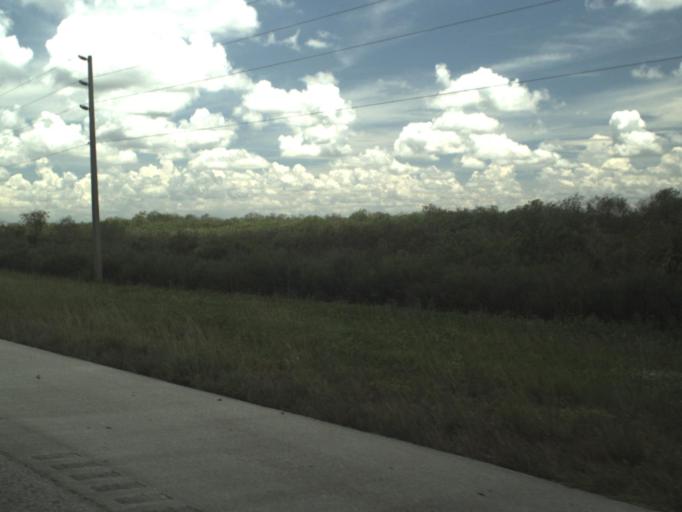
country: US
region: Florida
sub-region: Broward County
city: Weston
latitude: 26.1573
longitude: -80.7711
